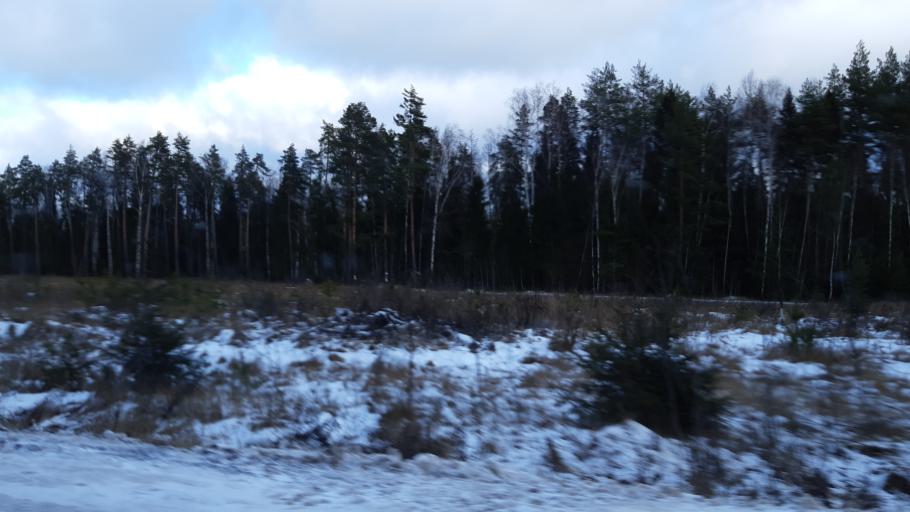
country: RU
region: Moskovskaya
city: Noginsk-9
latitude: 55.9654
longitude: 38.5400
